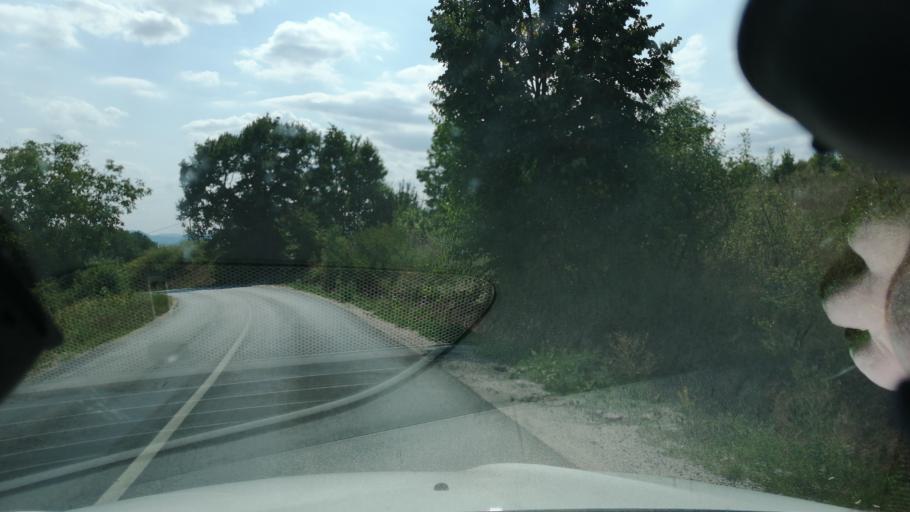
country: RS
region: Central Serbia
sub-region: Moravicki Okrug
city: Cacak
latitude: 43.8168
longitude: 20.2774
